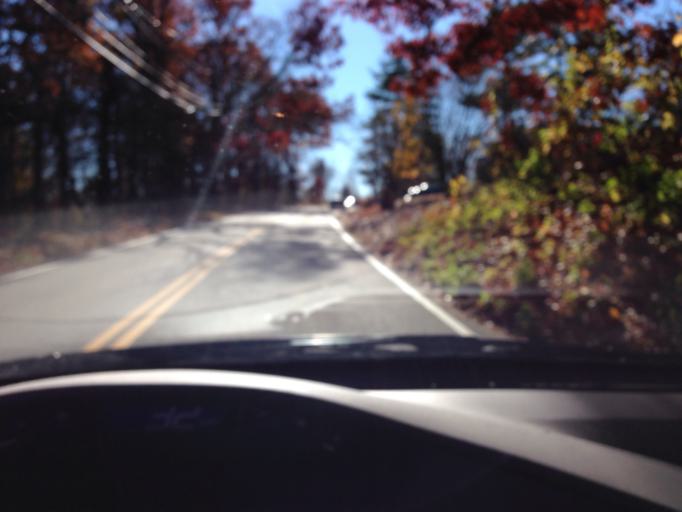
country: US
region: Massachusetts
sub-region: Middlesex County
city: Burlington
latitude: 42.4887
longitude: -71.2212
